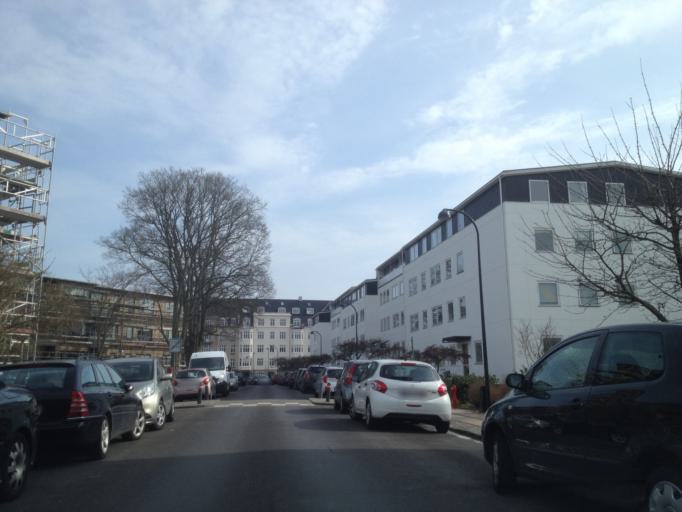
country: DK
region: Capital Region
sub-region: Gentofte Kommune
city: Charlottenlund
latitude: 55.7420
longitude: 12.5767
